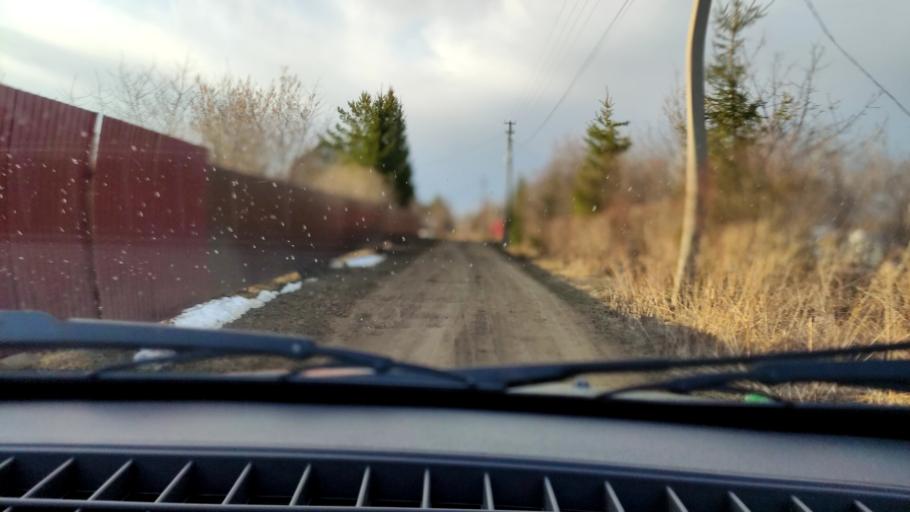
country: RU
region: Bashkortostan
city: Iglino
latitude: 54.8417
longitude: 56.4722
